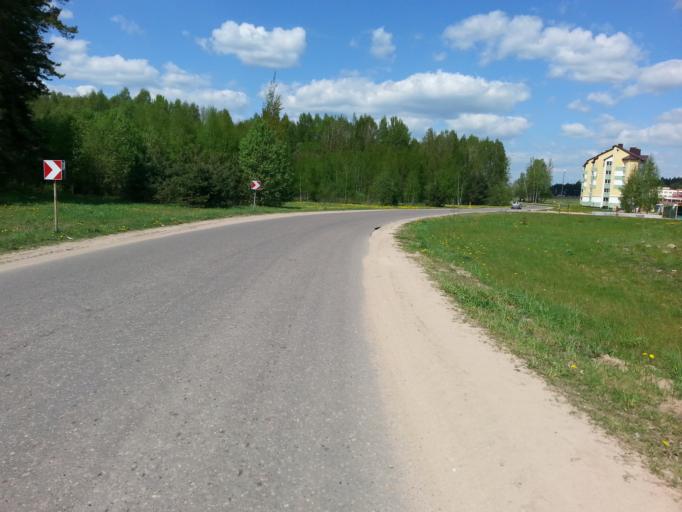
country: BY
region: Minsk
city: Narach
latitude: 54.9132
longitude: 26.6975
